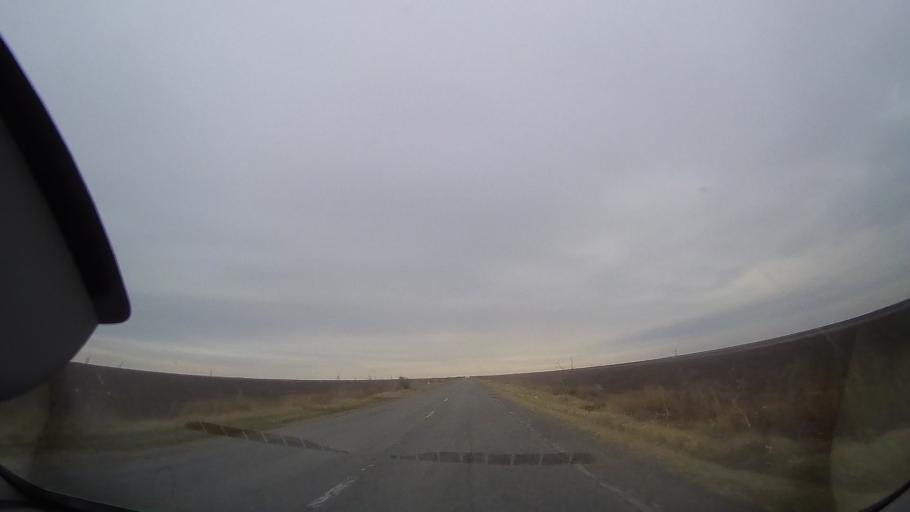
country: RO
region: Ialomita
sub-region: Oras Amara
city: Amara
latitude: 44.6520
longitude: 27.3006
